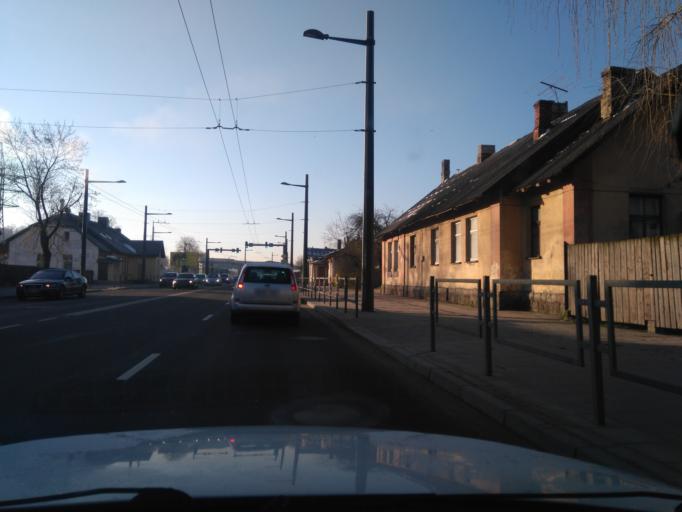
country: LT
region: Kauno apskritis
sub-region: Kaunas
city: Aleksotas
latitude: 54.8793
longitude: 23.9323
